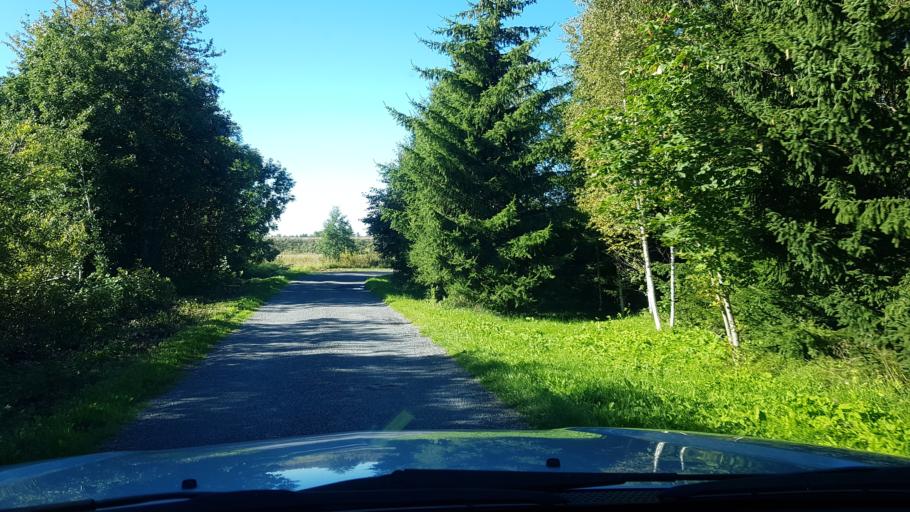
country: EE
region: Harju
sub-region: Joelaehtme vald
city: Loo
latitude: 59.4333
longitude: 24.9277
